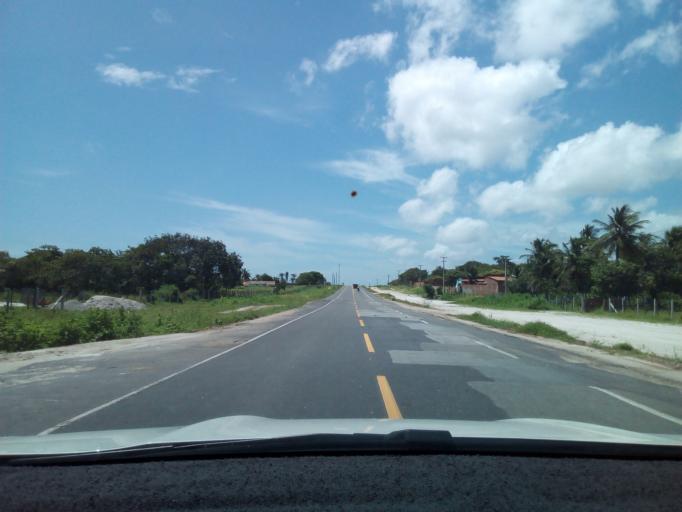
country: BR
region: Ceara
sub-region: Beberibe
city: Beberibe
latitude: -4.2631
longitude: -38.0647
